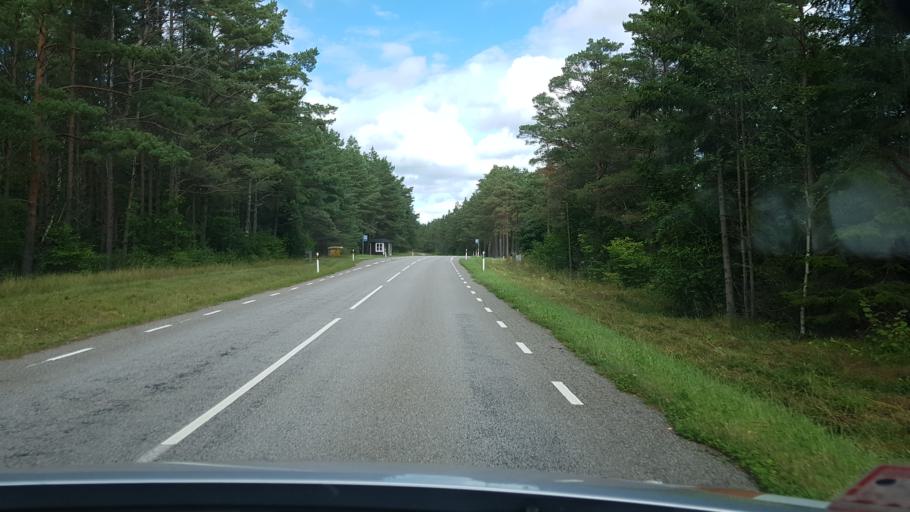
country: EE
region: Saare
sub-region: Kuressaare linn
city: Kuressaare
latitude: 57.9907
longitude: 22.1624
